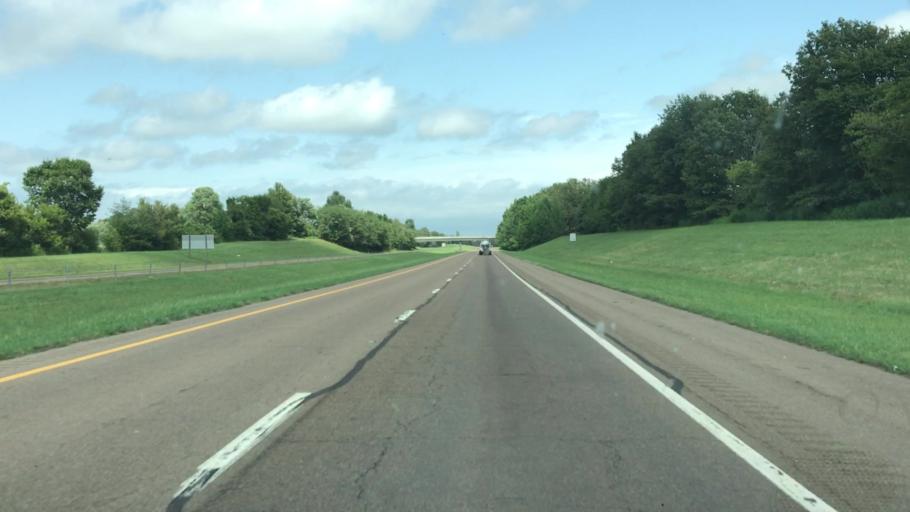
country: US
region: Tennessee
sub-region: Obion County
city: Union City
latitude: 36.4491
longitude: -89.0037
